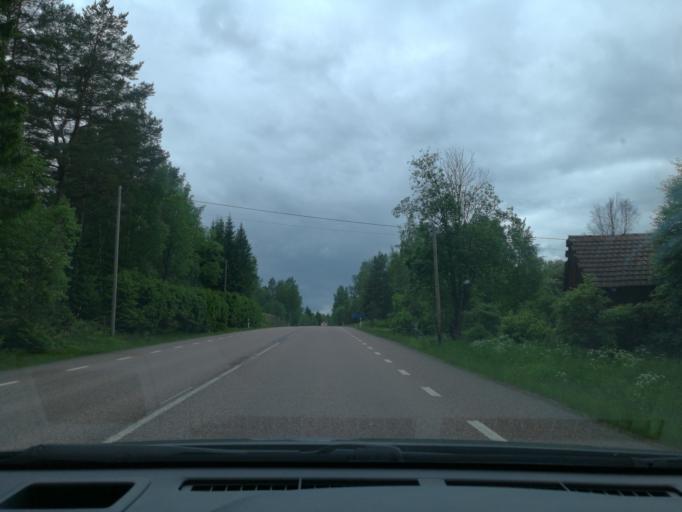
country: SE
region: Dalarna
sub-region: Smedjebackens Kommun
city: Smedjebacken
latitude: 60.1404
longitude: 15.3522
